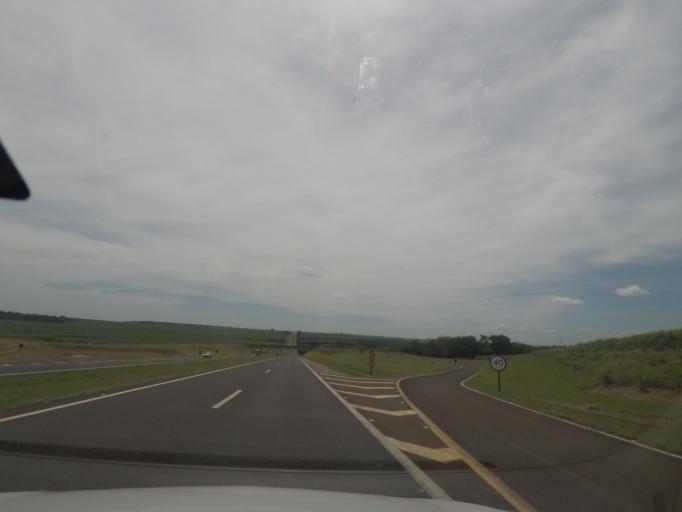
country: BR
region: Sao Paulo
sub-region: Bebedouro
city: Bebedouro
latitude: -21.0411
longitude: -48.4173
